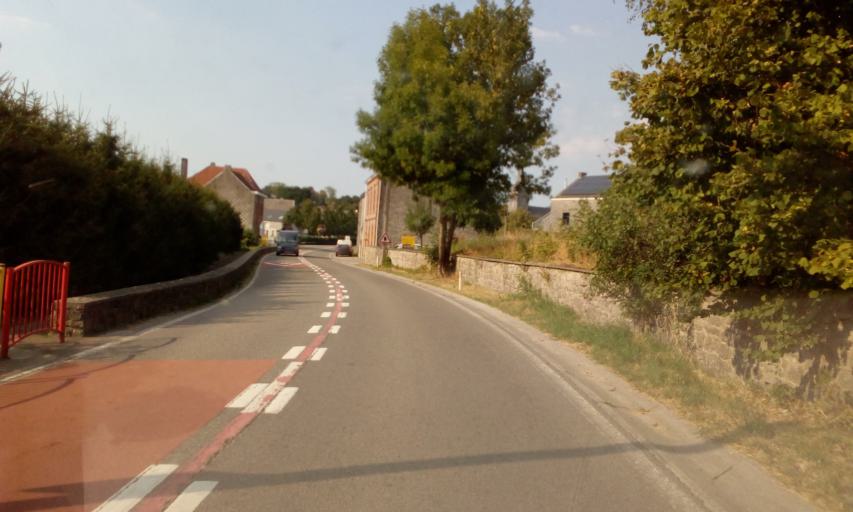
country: BE
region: Wallonia
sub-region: Province du Luxembourg
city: Tellin
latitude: 50.1195
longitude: 5.2481
